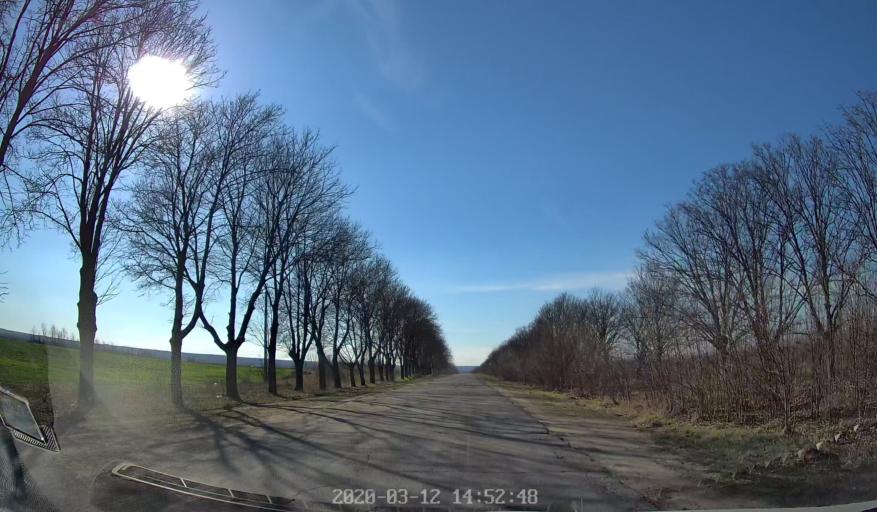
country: MD
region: Criuleni
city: Criuleni
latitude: 47.2194
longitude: 29.0917
